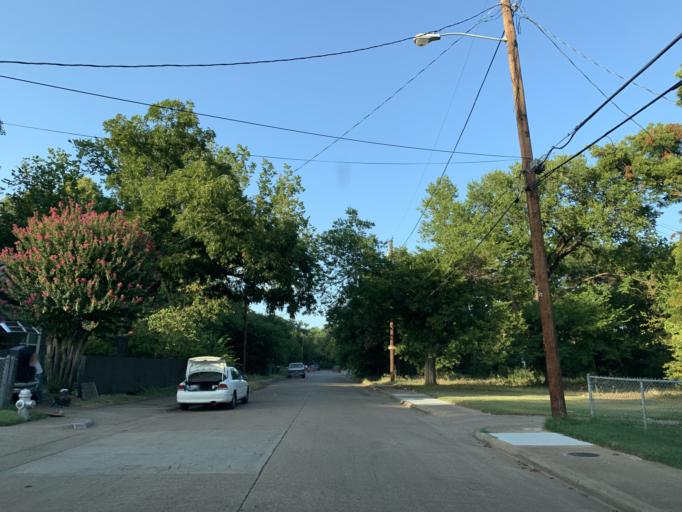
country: US
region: Texas
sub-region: Dallas County
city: Dallas
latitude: 32.7642
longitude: -96.7460
